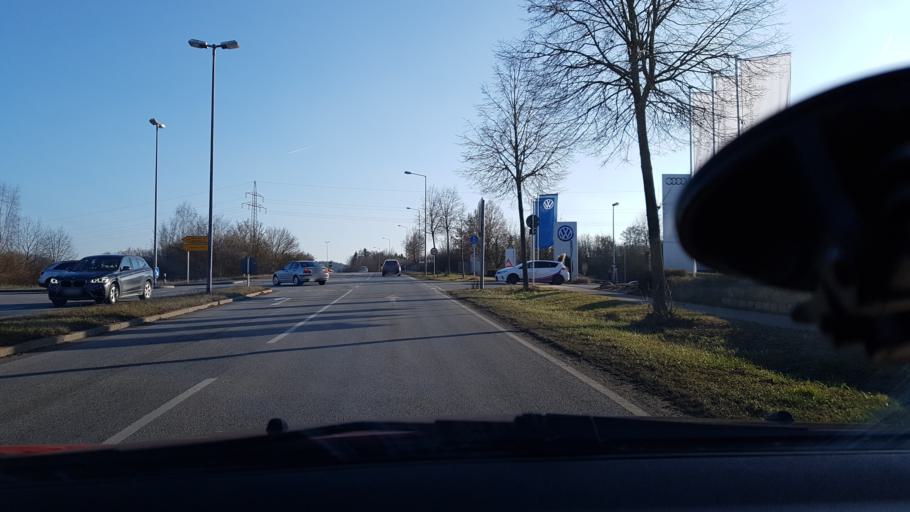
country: DE
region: Bavaria
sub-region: Lower Bavaria
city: Pfarrkirchen
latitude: 48.4173
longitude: 12.9452
